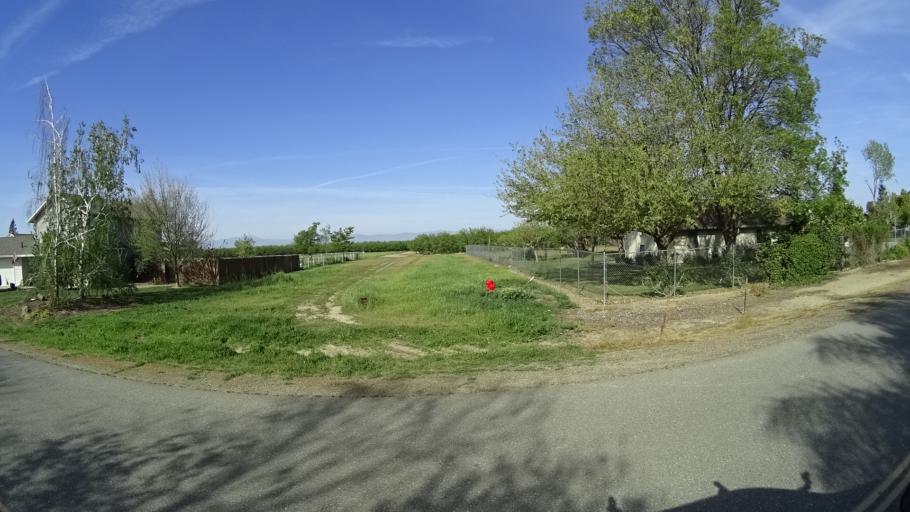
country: US
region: California
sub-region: Glenn County
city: Willows
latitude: 39.6141
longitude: -122.1954
